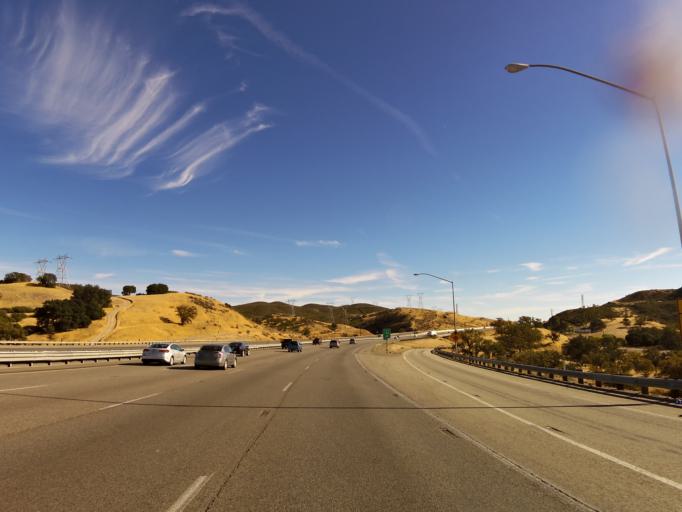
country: US
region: California
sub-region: Los Angeles County
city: Castaic
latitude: 34.5724
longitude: -118.6916
